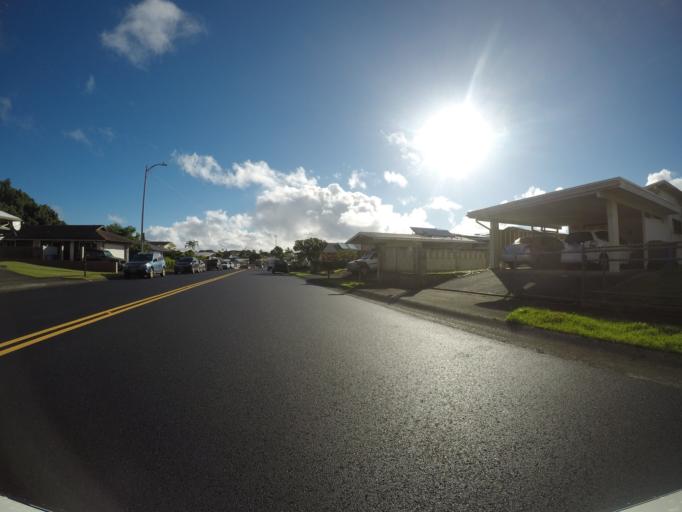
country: US
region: Hawaii
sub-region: Honolulu County
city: He'eia
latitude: 21.4220
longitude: -157.8111
